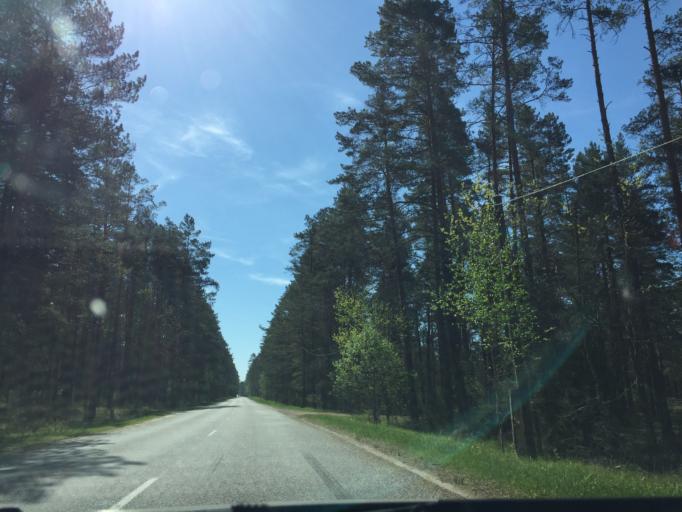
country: LV
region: Garkalne
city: Garkalne
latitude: 57.0240
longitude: 24.4330
